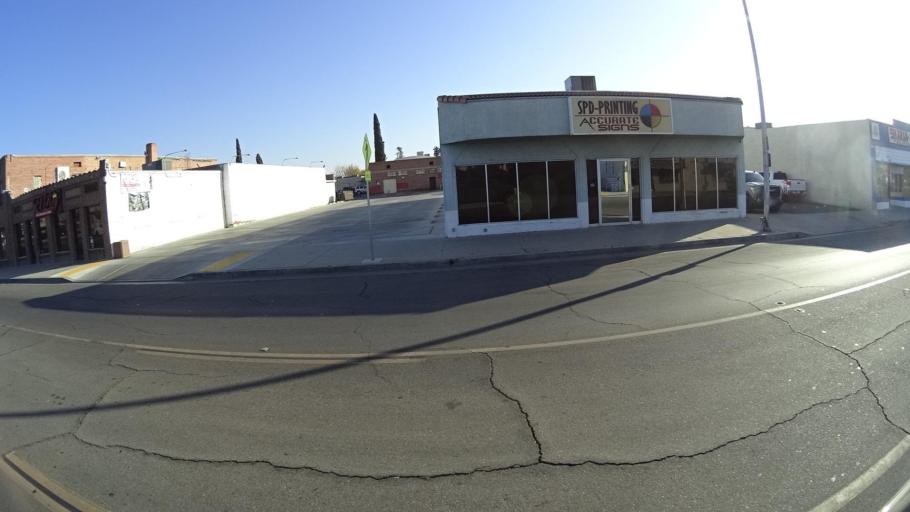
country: US
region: California
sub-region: Kern County
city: Delano
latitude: 35.7711
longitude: -119.2476
